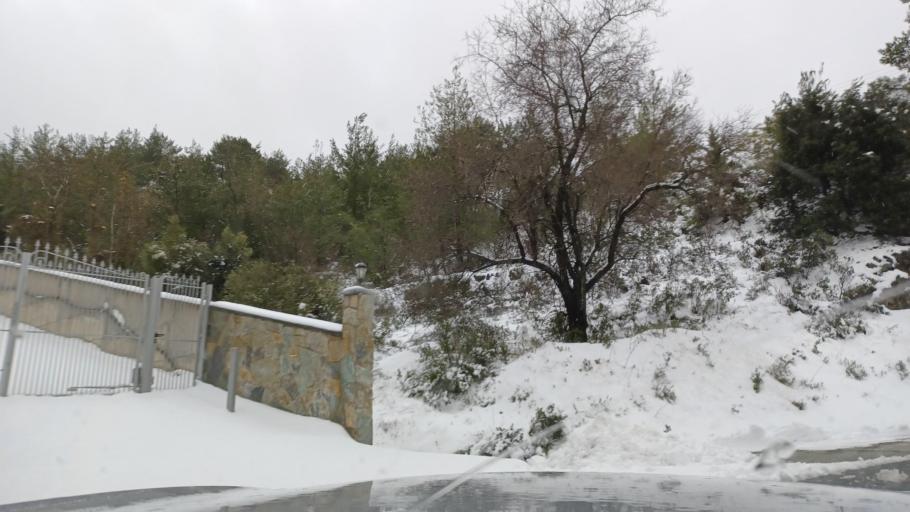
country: CY
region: Limassol
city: Pelendri
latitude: 34.9113
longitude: 32.9562
